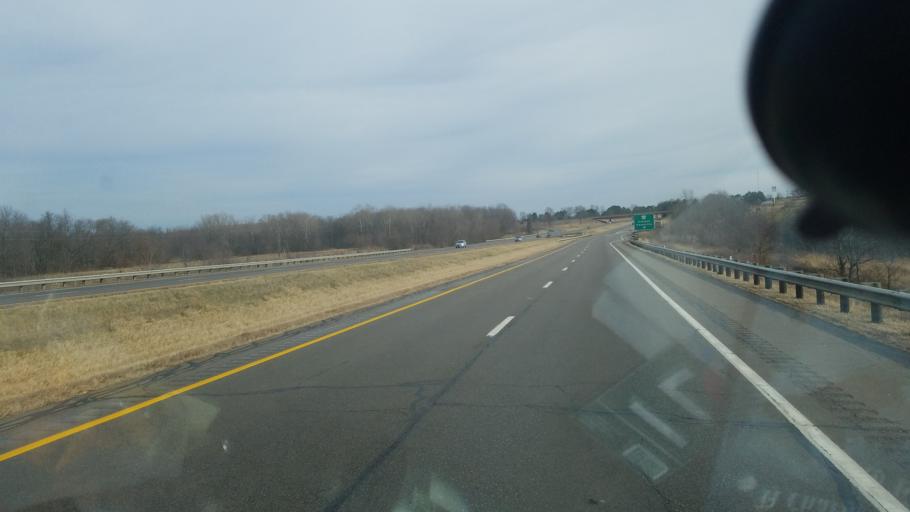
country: US
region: Ohio
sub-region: Ashland County
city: Ashland
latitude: 40.7851
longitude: -82.2715
